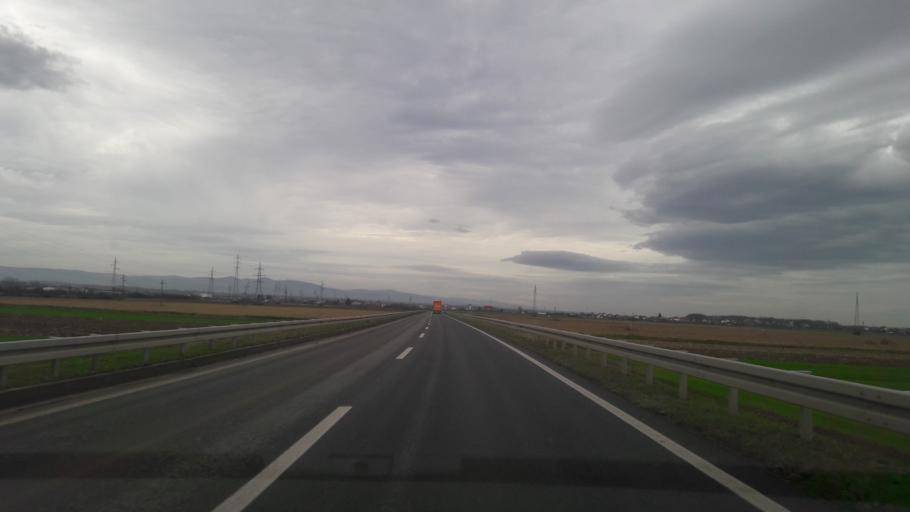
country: HR
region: Osjecko-Baranjska
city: Velimirovac
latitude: 45.5103
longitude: 18.1115
